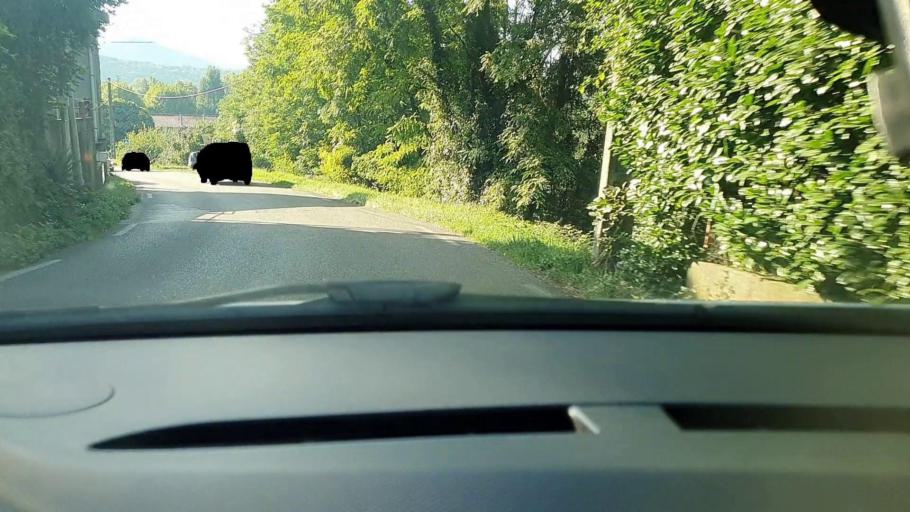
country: FR
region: Languedoc-Roussillon
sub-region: Departement du Gard
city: Besseges
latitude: 44.2872
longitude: 4.1242
